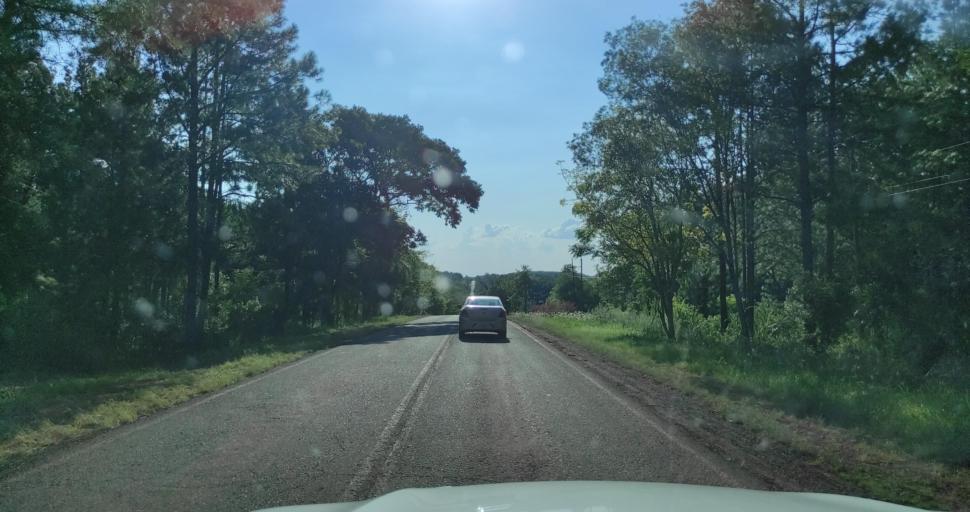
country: AR
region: Misiones
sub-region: Departamento de Eldorado
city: Eldorado
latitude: -26.3998
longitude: -54.3938
